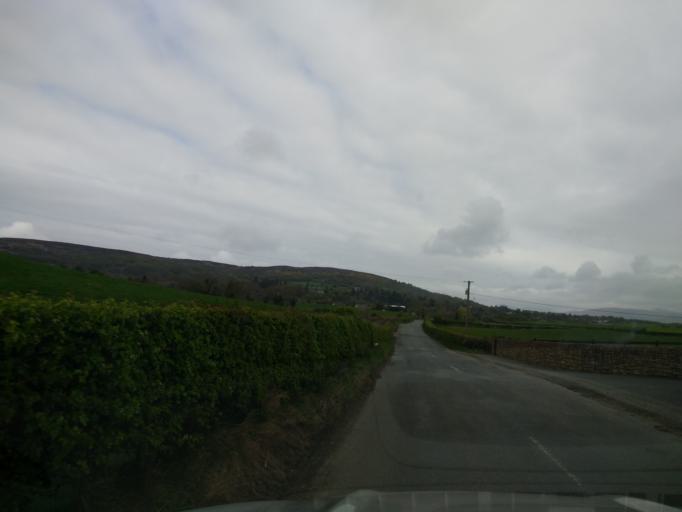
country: IE
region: Ulster
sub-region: County Donegal
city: Buncrana
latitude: 55.1045
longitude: -7.5347
